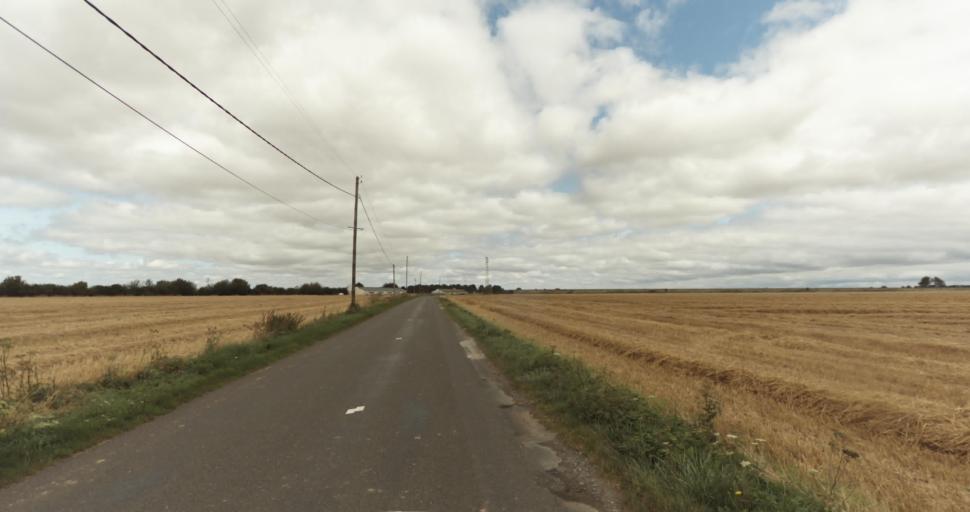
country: FR
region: Haute-Normandie
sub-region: Departement de l'Eure
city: Evreux
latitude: 48.9447
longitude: 1.1996
